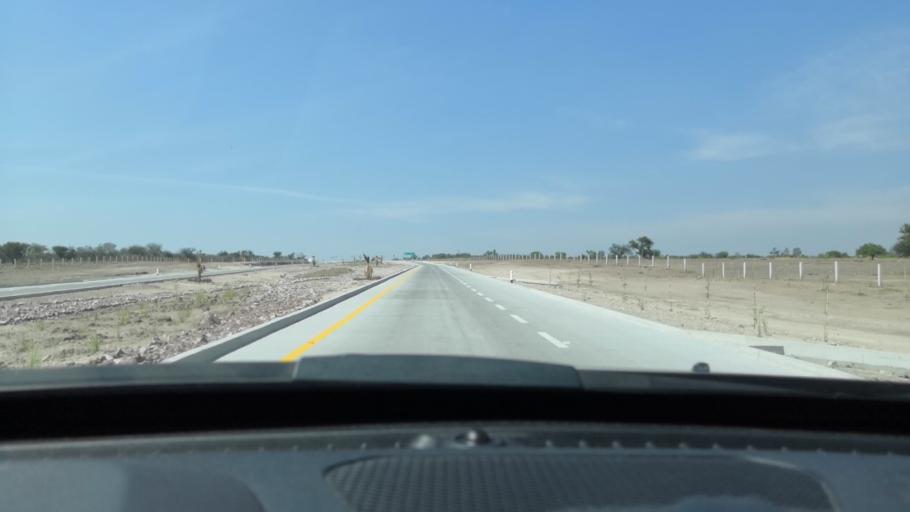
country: MX
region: Guanajuato
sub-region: Leon
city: Centro Familiar la Soledad
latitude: 21.0961
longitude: -101.7852
